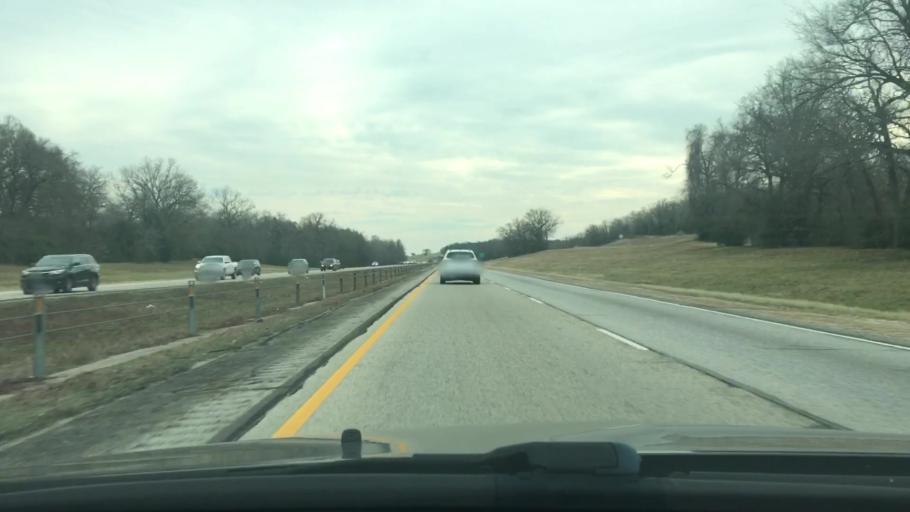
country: US
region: Texas
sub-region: Leon County
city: Centerville
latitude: 31.3029
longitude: -96.0005
